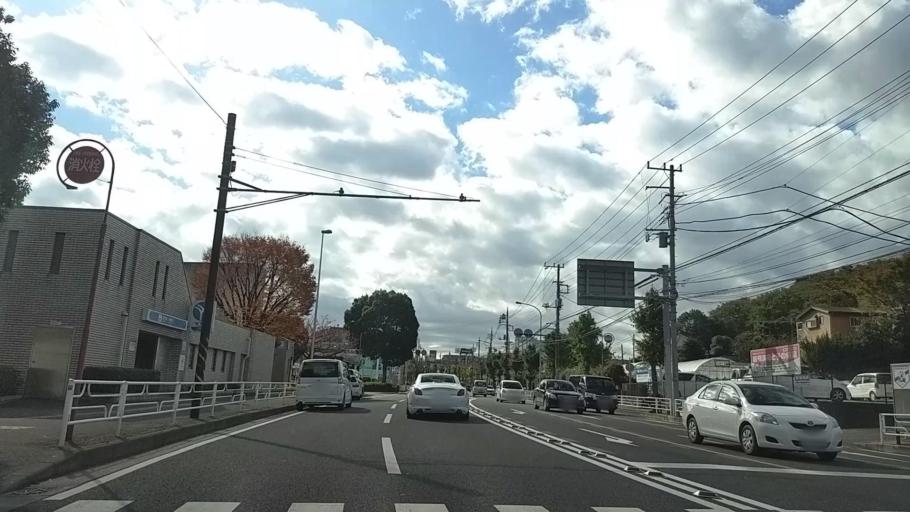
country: JP
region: Kanagawa
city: Yokohama
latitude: 35.4907
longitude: 139.6070
